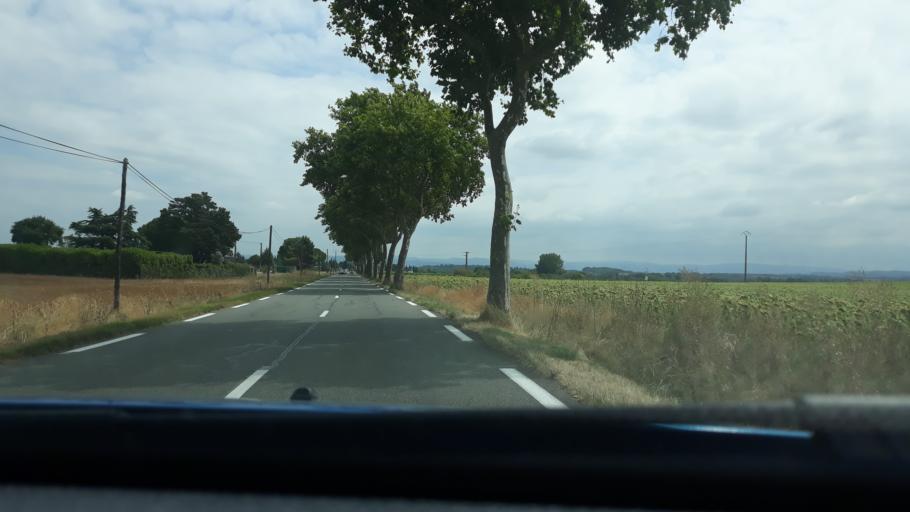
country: FR
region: Languedoc-Roussillon
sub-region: Departement de l'Aude
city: Pezens
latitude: 43.2631
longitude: 2.2441
